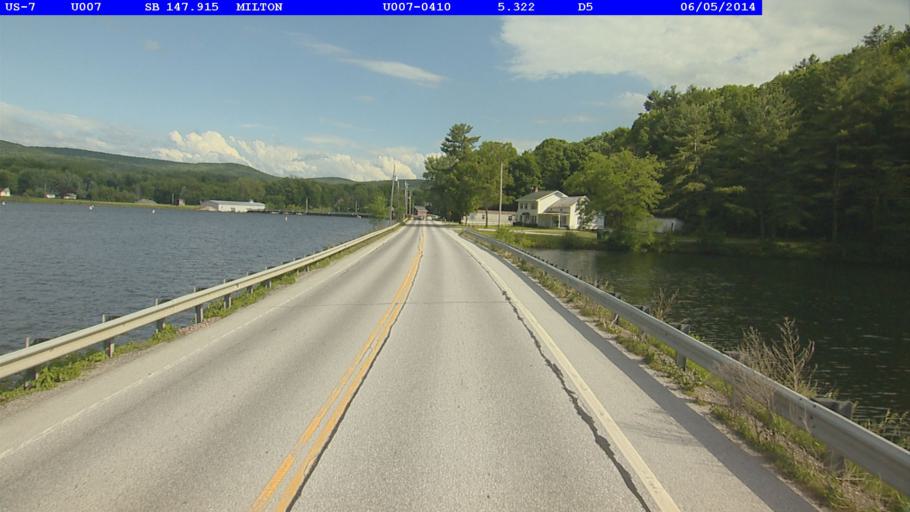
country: US
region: Vermont
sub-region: Chittenden County
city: Milton
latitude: 44.6435
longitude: -73.1160
